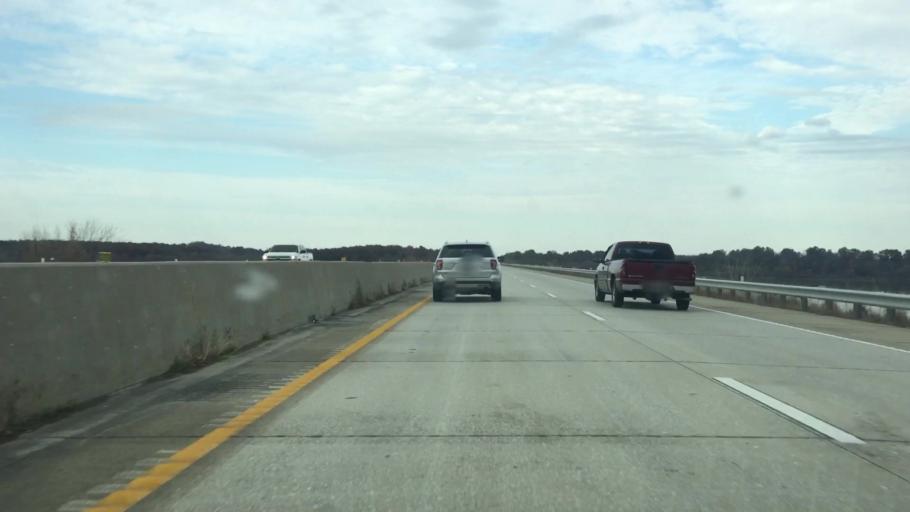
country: US
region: Missouri
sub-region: Henry County
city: Clinton
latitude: 38.2807
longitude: -93.7595
